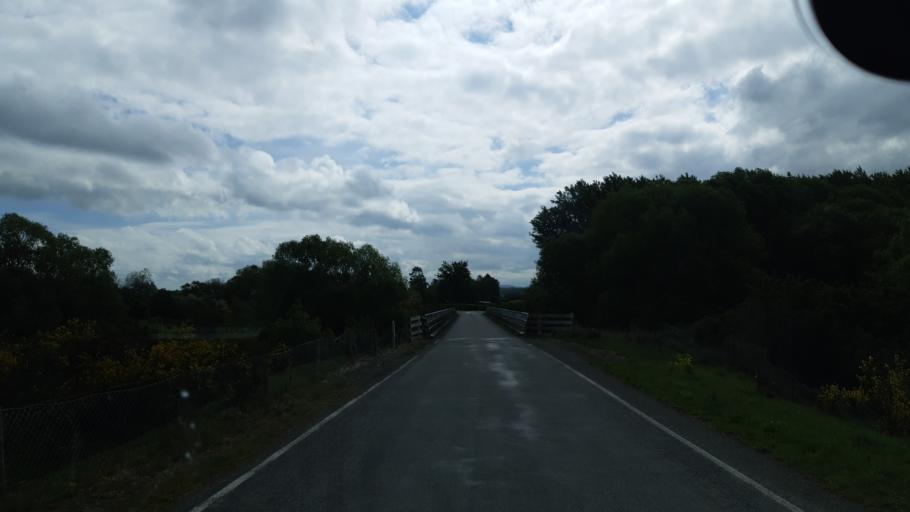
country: NZ
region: Canterbury
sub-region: Timaru District
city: Pleasant Point
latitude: -44.1723
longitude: 171.2146
